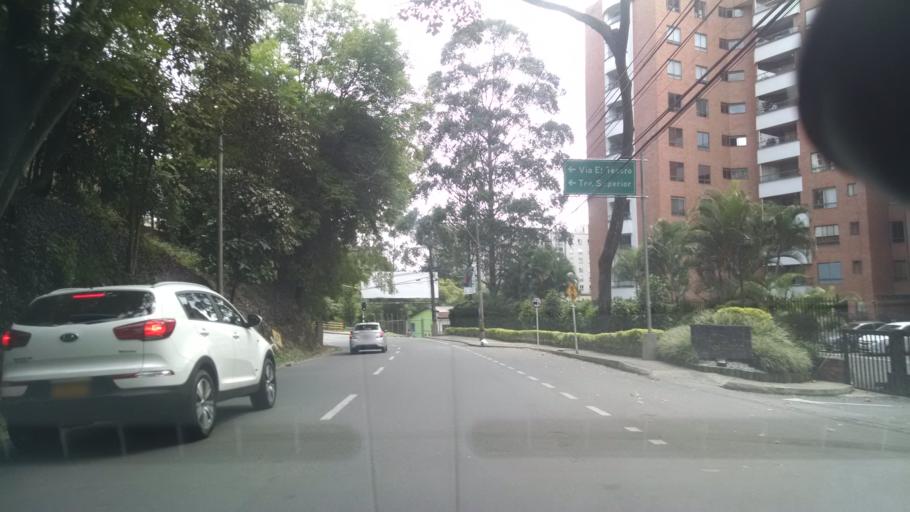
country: CO
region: Antioquia
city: Envigado
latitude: 6.2057
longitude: -75.5608
